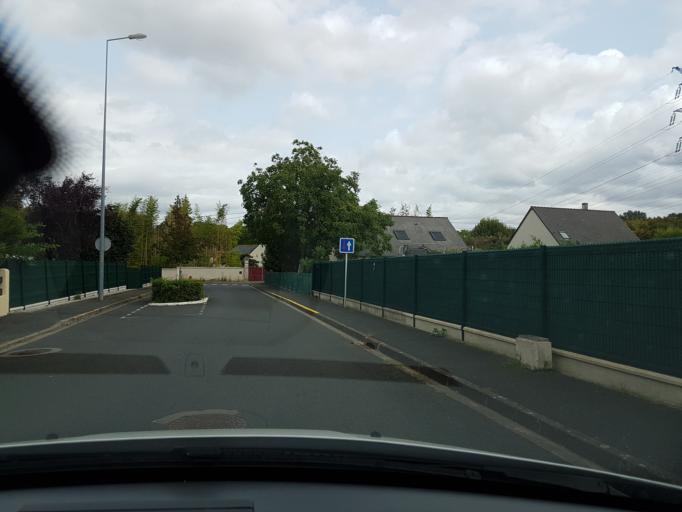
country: FR
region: Centre
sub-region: Departement d'Indre-et-Loire
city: Saint-Avertin
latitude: 47.3521
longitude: 0.7475
